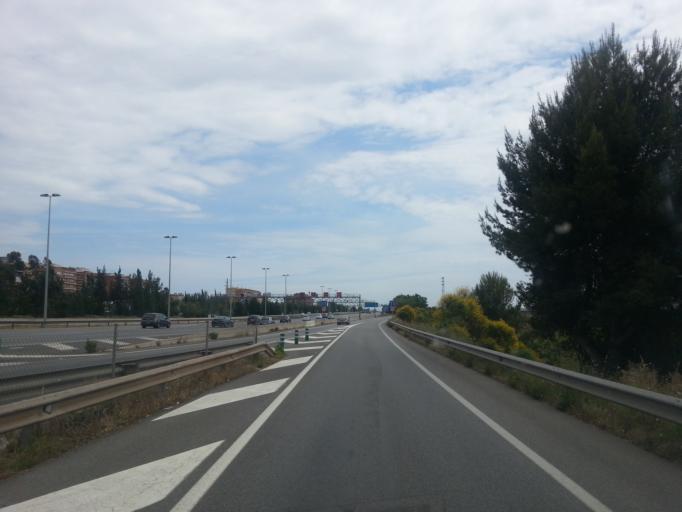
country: ES
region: Catalonia
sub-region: Provincia de Barcelona
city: Molins de Rei
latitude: 41.4188
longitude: 2.0085
